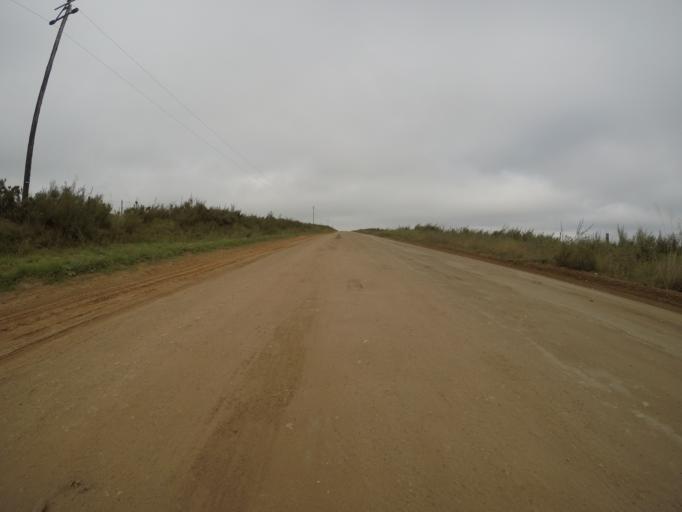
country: ZA
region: Eastern Cape
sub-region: Cacadu District Municipality
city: Kareedouw
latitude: -34.0201
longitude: 24.2397
